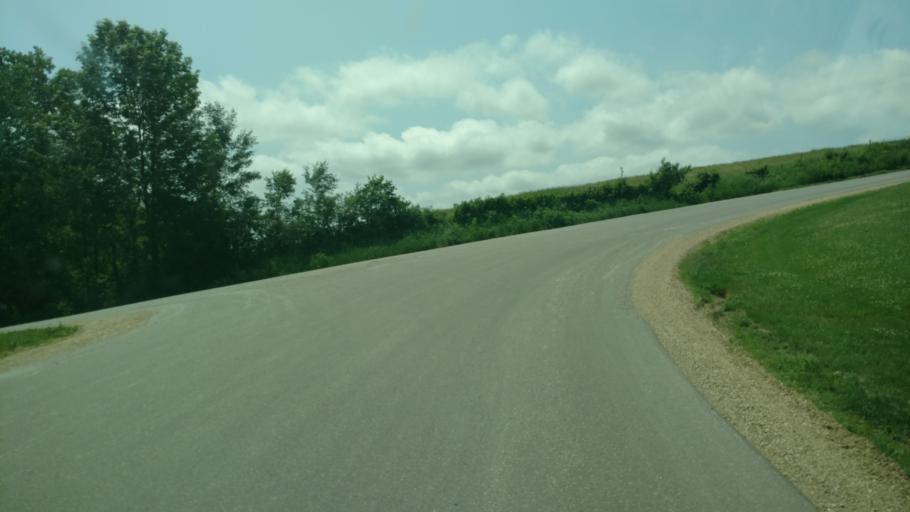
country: US
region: Wisconsin
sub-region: Monroe County
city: Cashton
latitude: 43.6969
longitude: -90.7253
